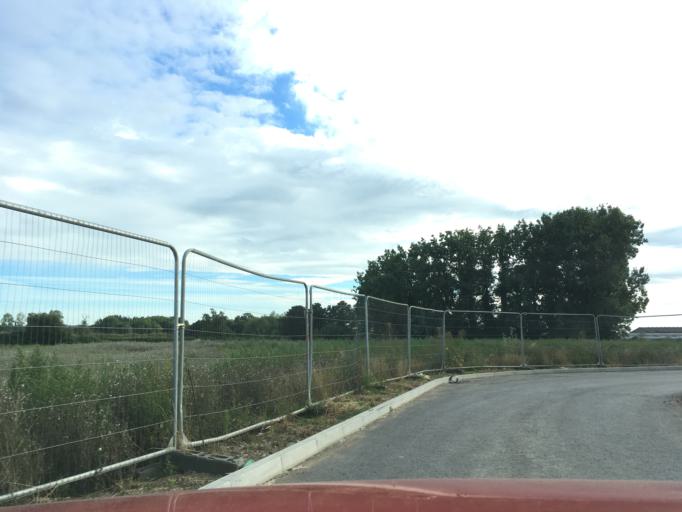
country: GB
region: England
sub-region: Gloucestershire
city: Stonehouse
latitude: 51.8055
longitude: -2.2757
